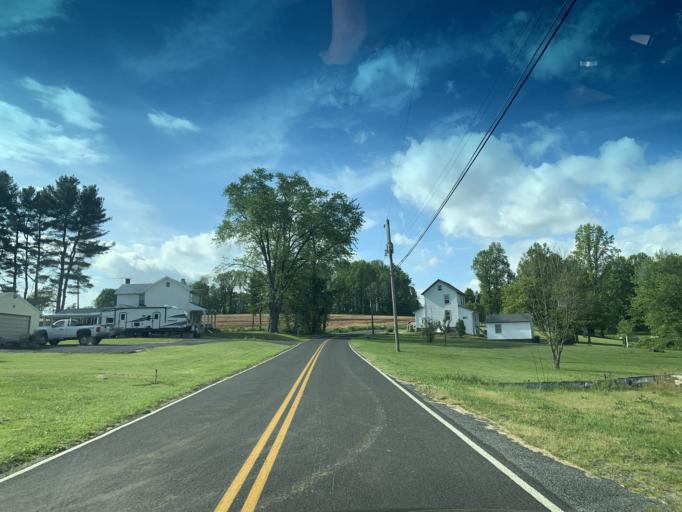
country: US
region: Maryland
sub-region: Cecil County
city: Rising Sun
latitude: 39.6997
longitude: -76.2016
